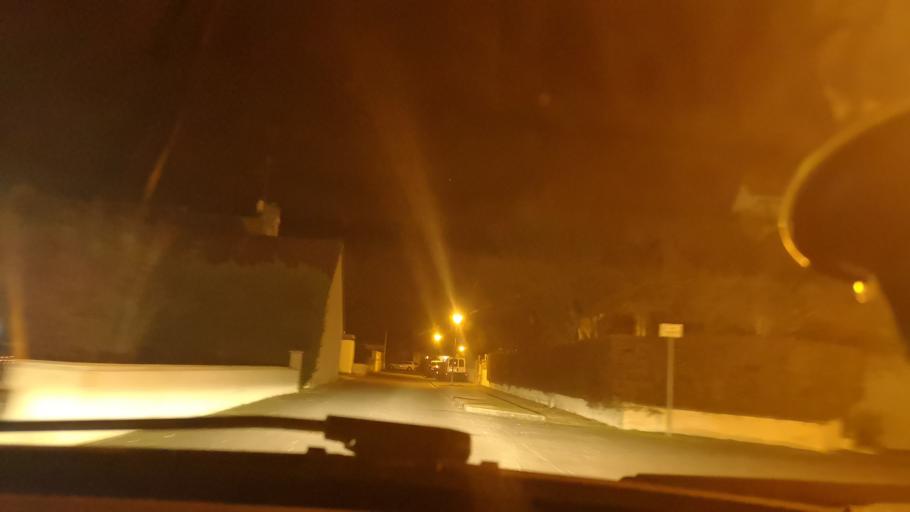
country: FR
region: Bourgogne
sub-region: Departement de Saone-et-Loire
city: Saint-Remy
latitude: 46.7671
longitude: 4.8259
